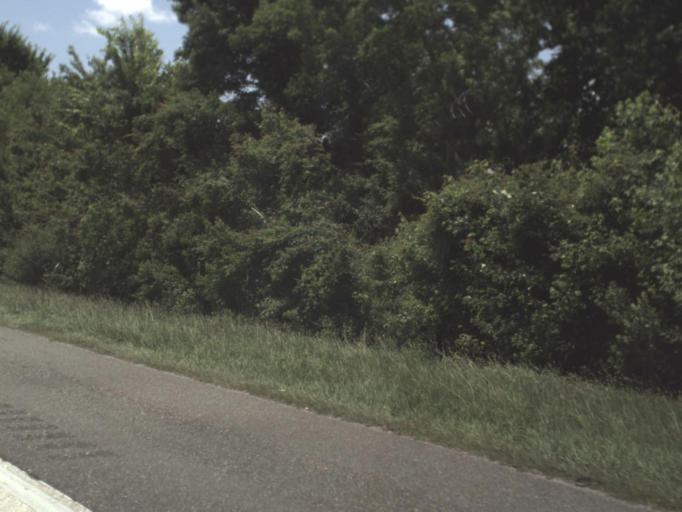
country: US
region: Florida
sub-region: Duval County
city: Jacksonville
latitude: 30.4164
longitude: -81.6571
